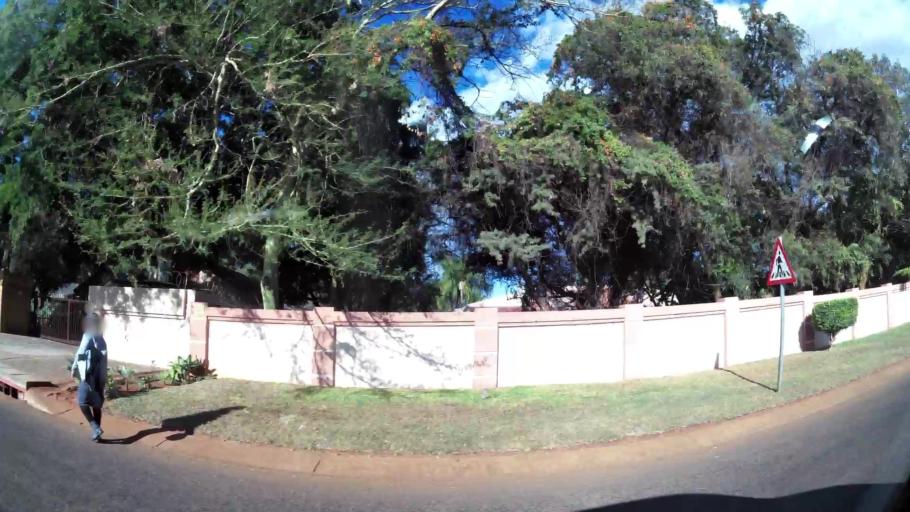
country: ZA
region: Limpopo
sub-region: Waterberg District Municipality
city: Mokopane
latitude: -24.2020
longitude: 29.0017
